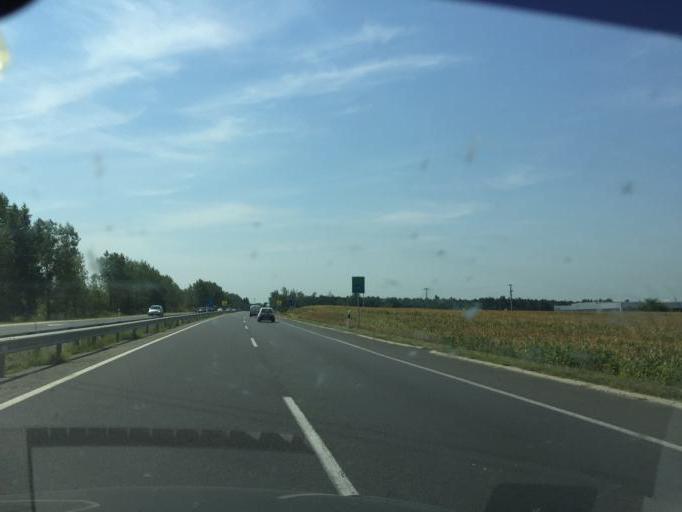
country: HU
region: Pest
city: God
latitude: 47.6809
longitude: 19.1736
